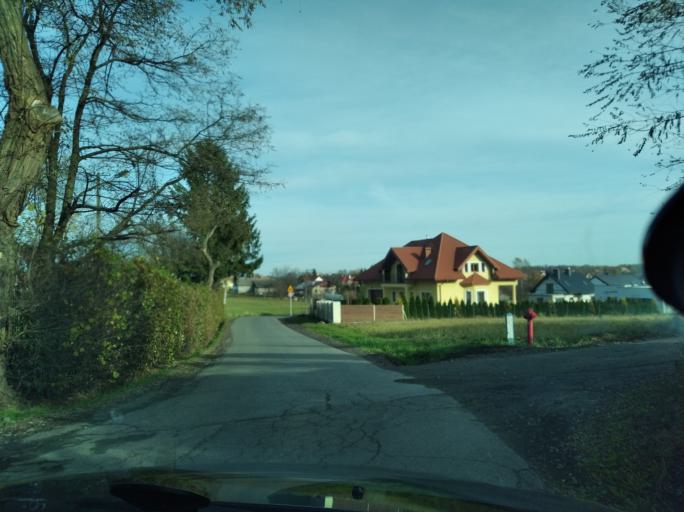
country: PL
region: Subcarpathian Voivodeship
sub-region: Powiat rzeszowski
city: Tyczyn
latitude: 49.9986
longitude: 22.0675
